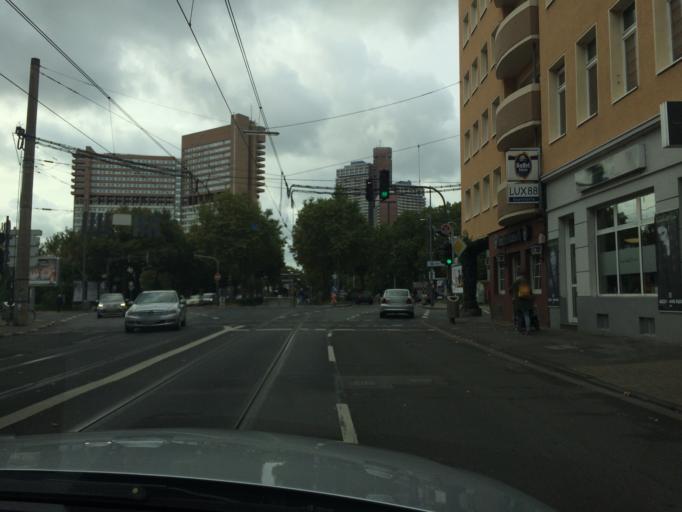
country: DE
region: North Rhine-Westphalia
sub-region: Regierungsbezirk Koln
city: Neustadt/Sued
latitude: 50.9255
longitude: 6.9377
